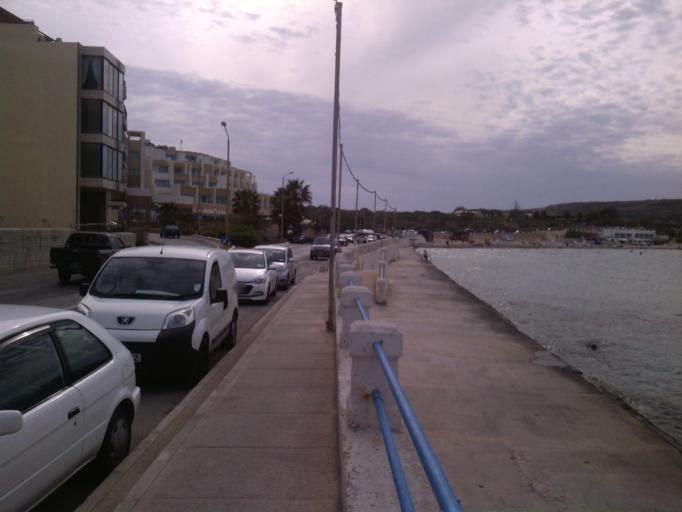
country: MT
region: Il-Mellieha
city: Mellieha
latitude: 35.9661
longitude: 14.3555
